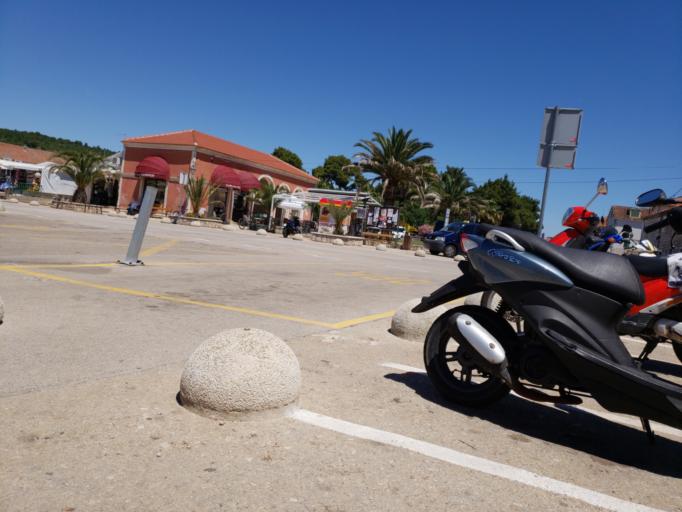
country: HR
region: Splitsko-Dalmatinska
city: Stari Grad
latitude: 43.1842
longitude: 16.5989
